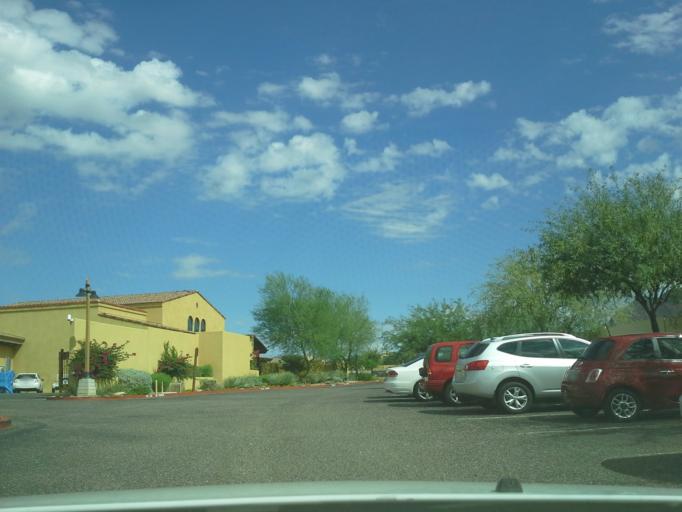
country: US
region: Arizona
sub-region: Maricopa County
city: Paradise Valley
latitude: 33.6557
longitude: -111.8650
